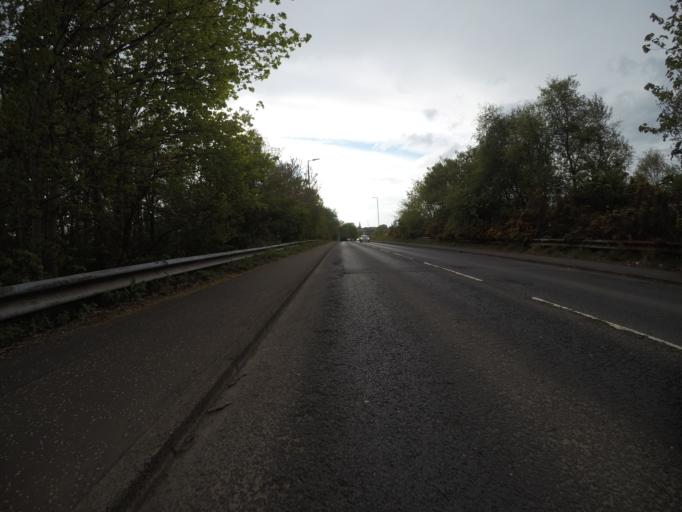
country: GB
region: Scotland
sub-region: North Ayrshire
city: Irvine
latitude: 55.6098
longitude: -4.6475
